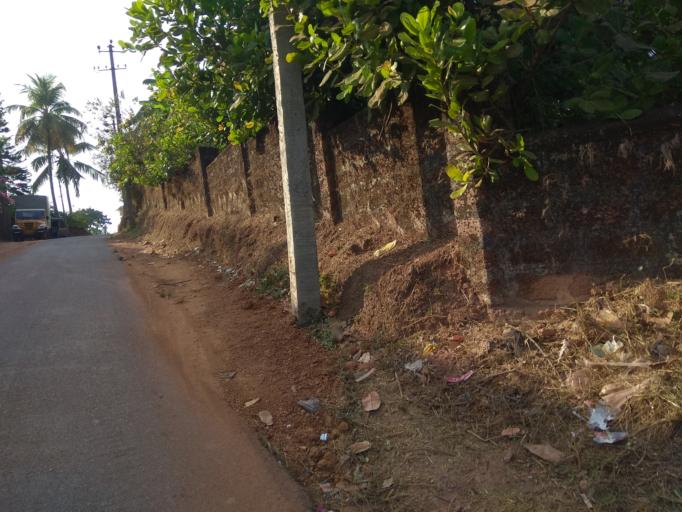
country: IN
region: Karnataka
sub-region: Dakshina Kannada
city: Mangalore
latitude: 12.9232
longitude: 74.8703
